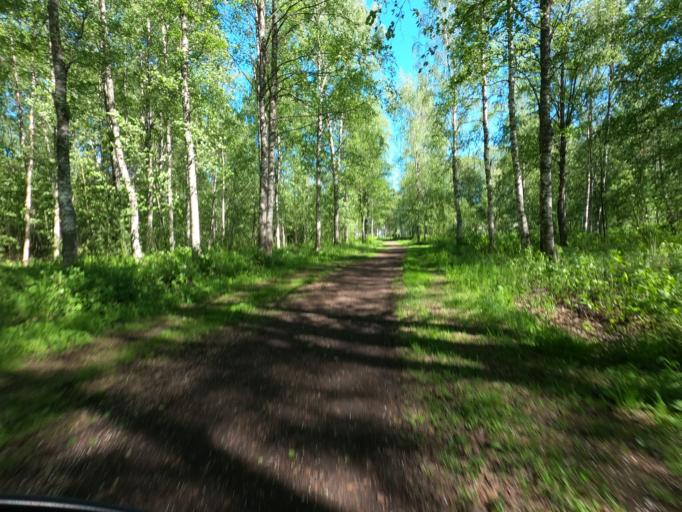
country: FI
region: North Karelia
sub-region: Joensuu
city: Joensuu
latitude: 62.6050
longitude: 29.8148
